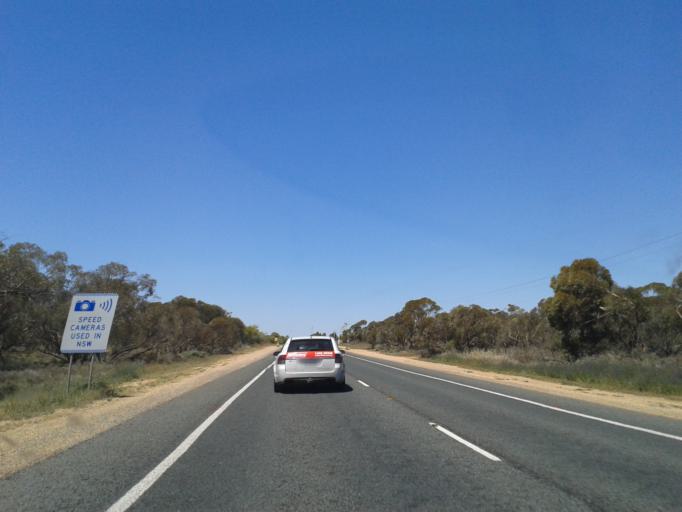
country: AU
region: New South Wales
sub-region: Wentworth
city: Gol Gol
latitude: -34.1988
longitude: 142.2419
